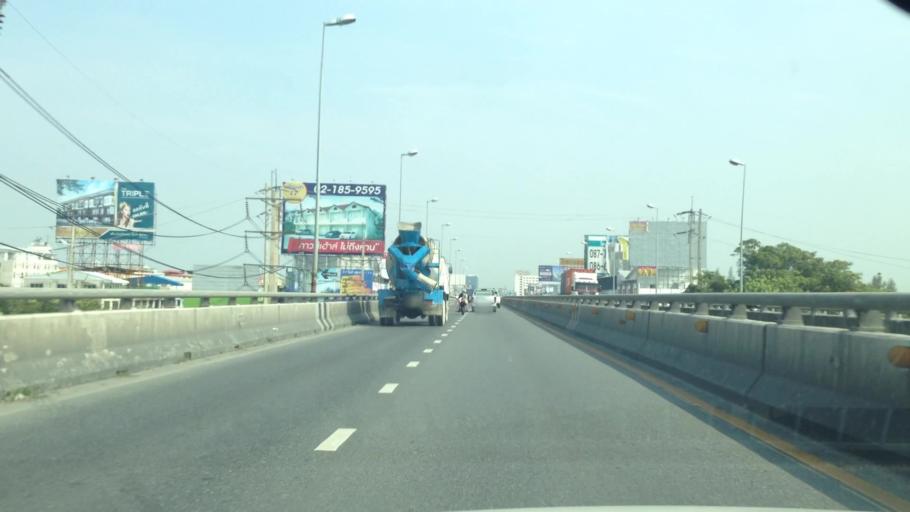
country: TH
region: Bangkok
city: Bang Na
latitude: 13.6285
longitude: 100.6273
